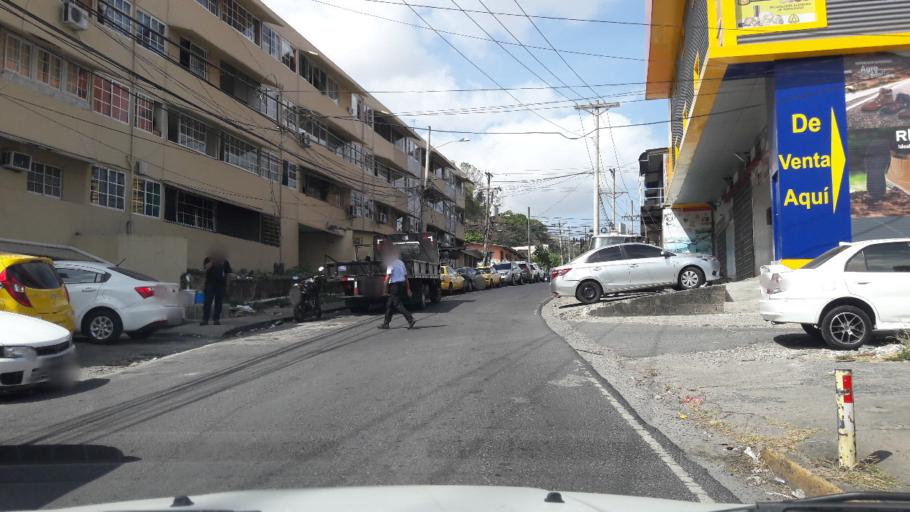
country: PA
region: Panama
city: San Miguelito
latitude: 9.0333
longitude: -79.4914
